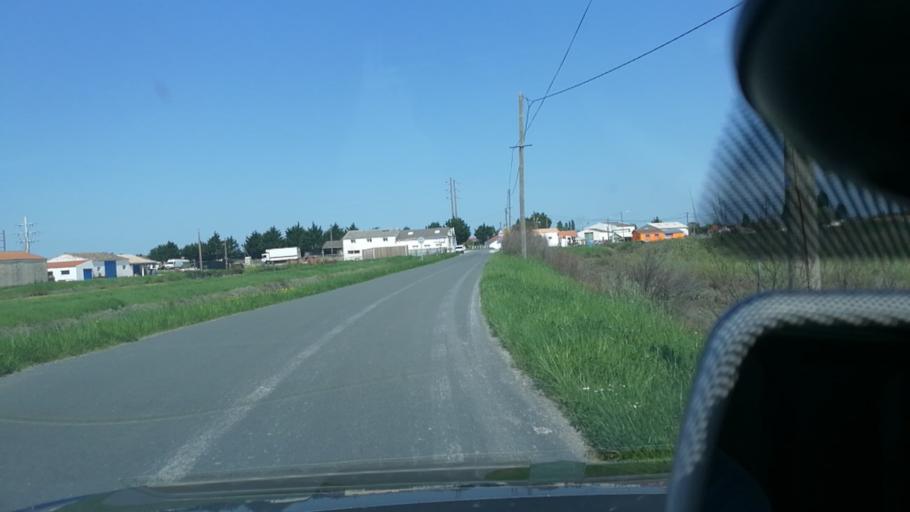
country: FR
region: Poitou-Charentes
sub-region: Departement de la Charente-Maritime
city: Saint-Trojan-les-Bains
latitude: 45.8689
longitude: -1.2199
